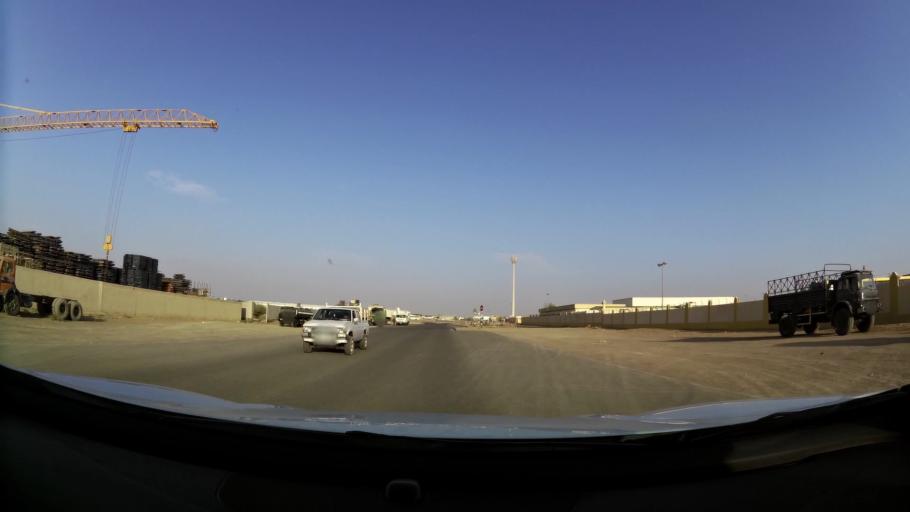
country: AE
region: Abu Dhabi
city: Al Ain
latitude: 24.1370
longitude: 55.8203
